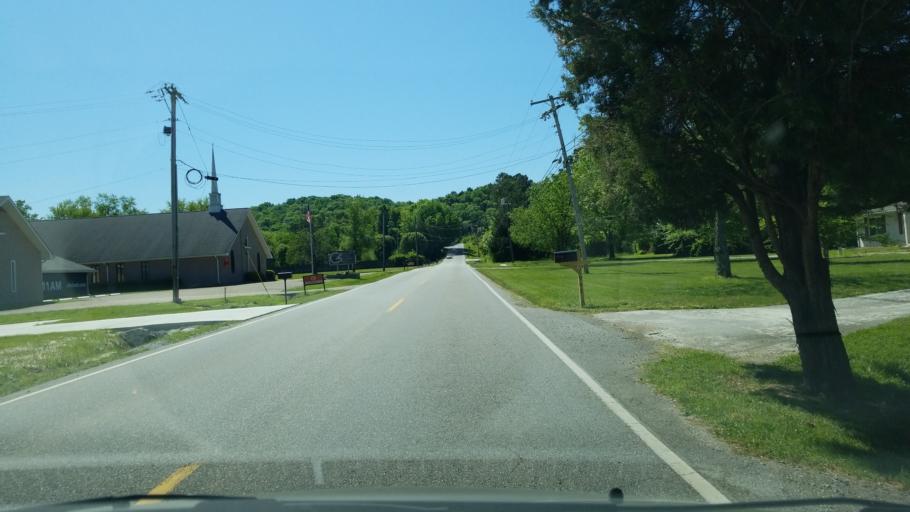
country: US
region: Tennessee
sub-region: Hamilton County
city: Middle Valley
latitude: 35.1752
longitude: -85.1788
